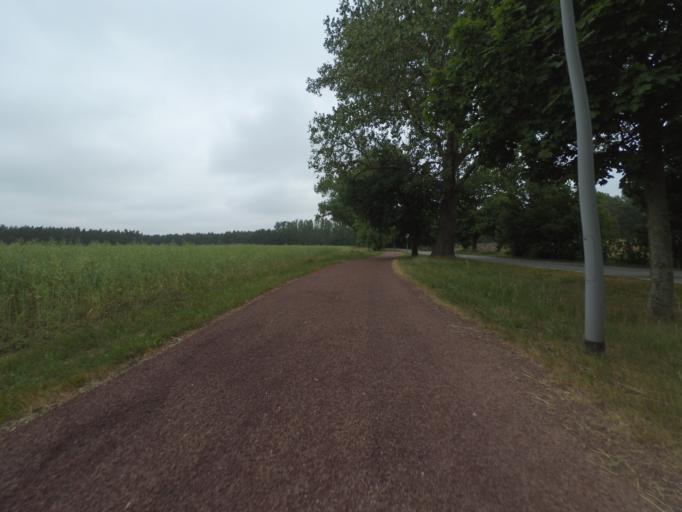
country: DE
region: Mecklenburg-Vorpommern
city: Plau am See
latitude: 53.4735
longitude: 12.2805
